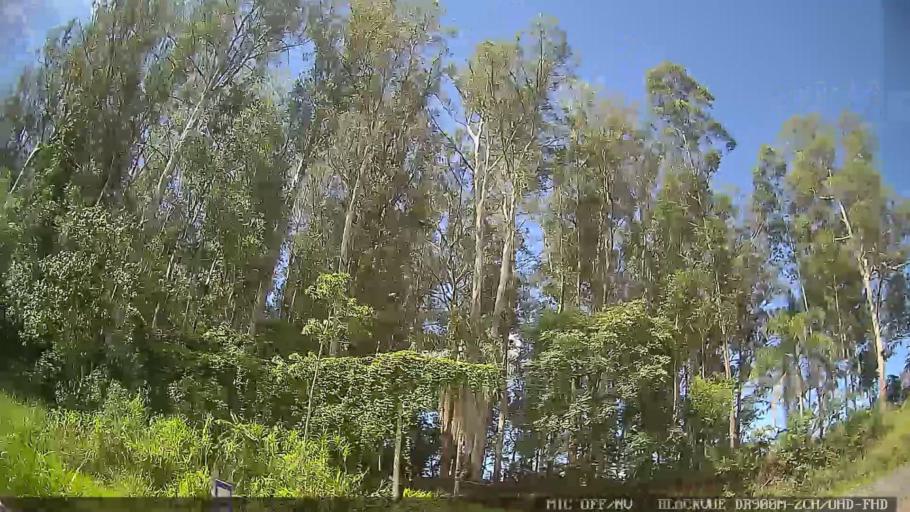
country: BR
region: Sao Paulo
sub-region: Amparo
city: Amparo
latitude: -22.7096
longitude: -46.8341
